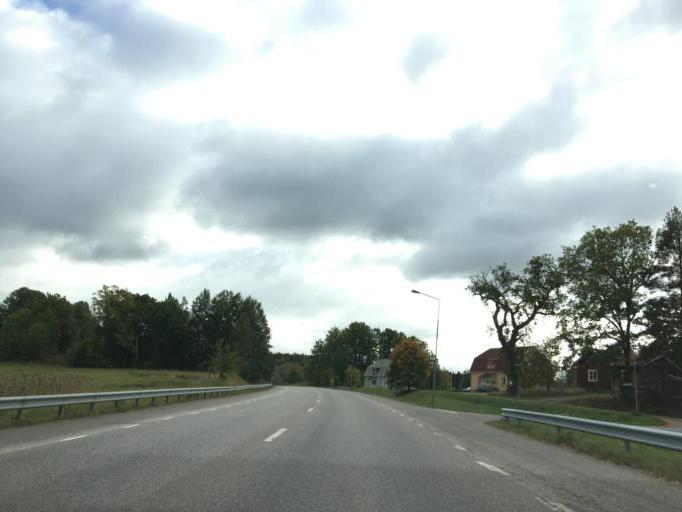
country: SE
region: Soedermanland
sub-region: Nykopings Kommun
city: Olstorp
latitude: 58.8581
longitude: 16.7008
